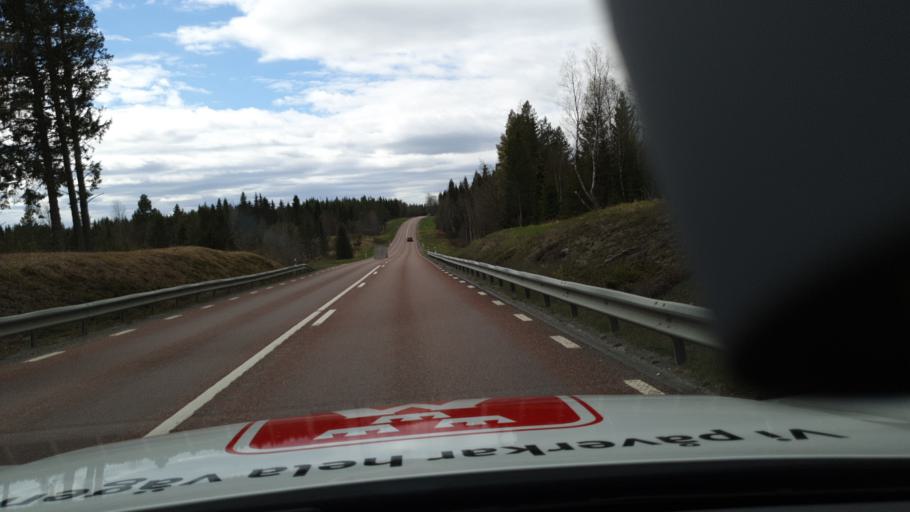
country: SE
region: Jaemtland
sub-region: OEstersunds Kommun
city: Brunflo
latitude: 63.0056
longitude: 14.6788
